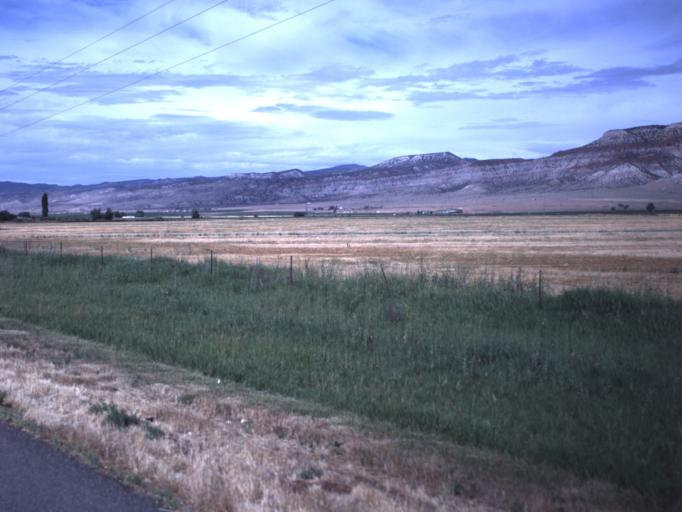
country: US
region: Utah
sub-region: Sevier County
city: Richfield
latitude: 38.8226
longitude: -112.0004
